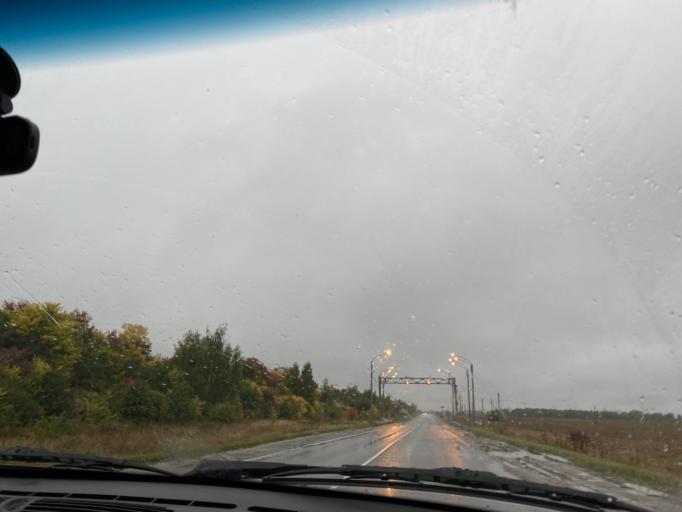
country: RU
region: Rjazan
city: Ryazan'
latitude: 54.4714
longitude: 39.8508
